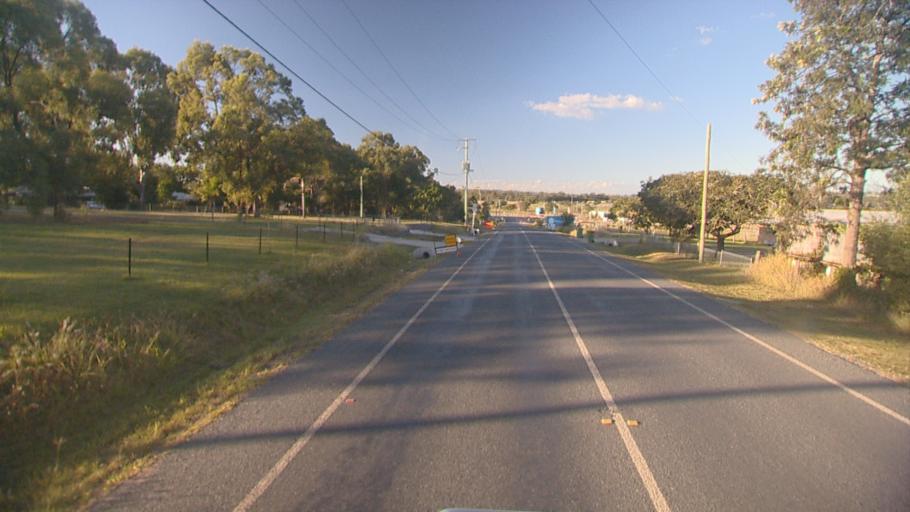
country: AU
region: Queensland
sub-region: Logan
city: Logan Reserve
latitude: -27.7188
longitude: 153.1126
